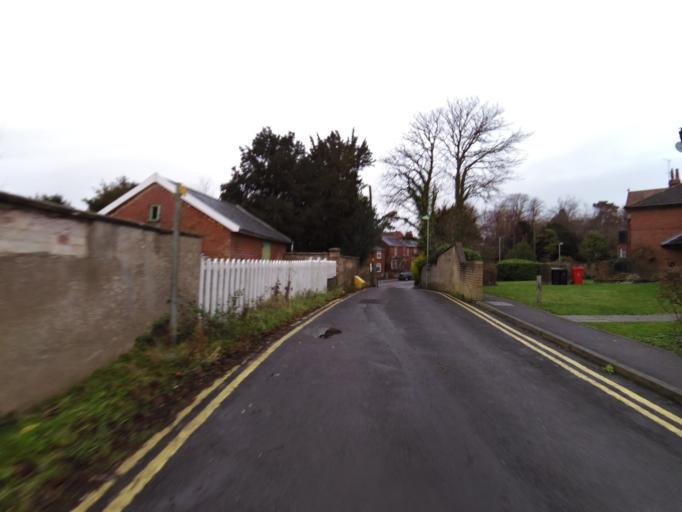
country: GB
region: England
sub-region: Suffolk
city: Stowmarket
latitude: 52.1820
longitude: 0.9998
